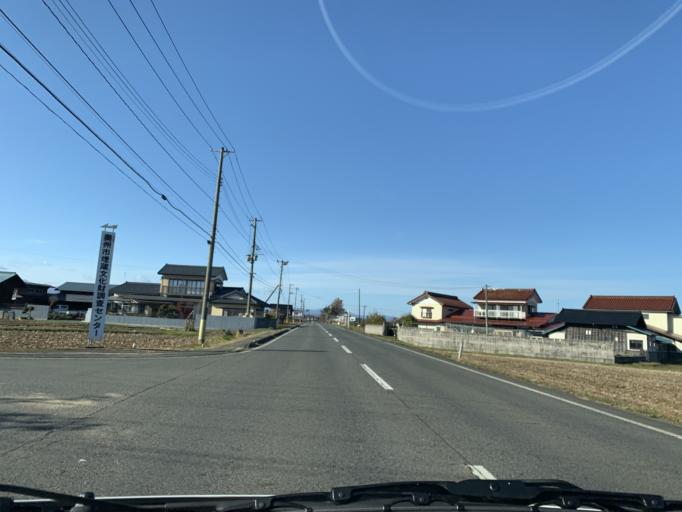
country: JP
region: Iwate
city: Mizusawa
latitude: 39.1767
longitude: 141.1371
